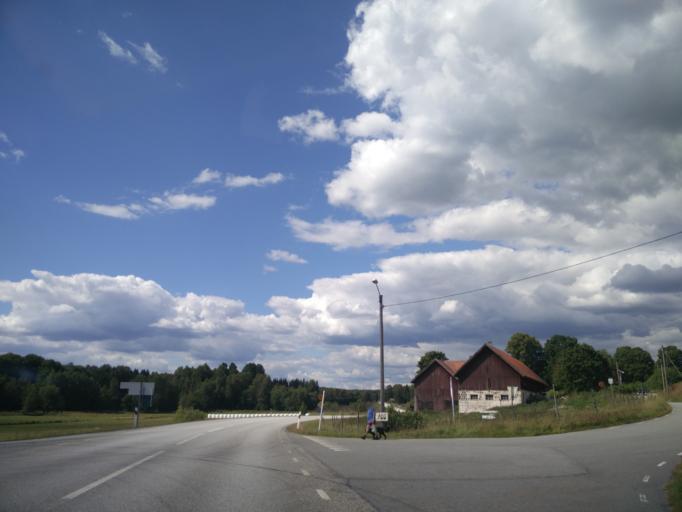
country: SE
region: OErebro
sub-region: Ljusnarsbergs Kommun
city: Kopparberg
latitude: 59.7814
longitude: 14.7807
